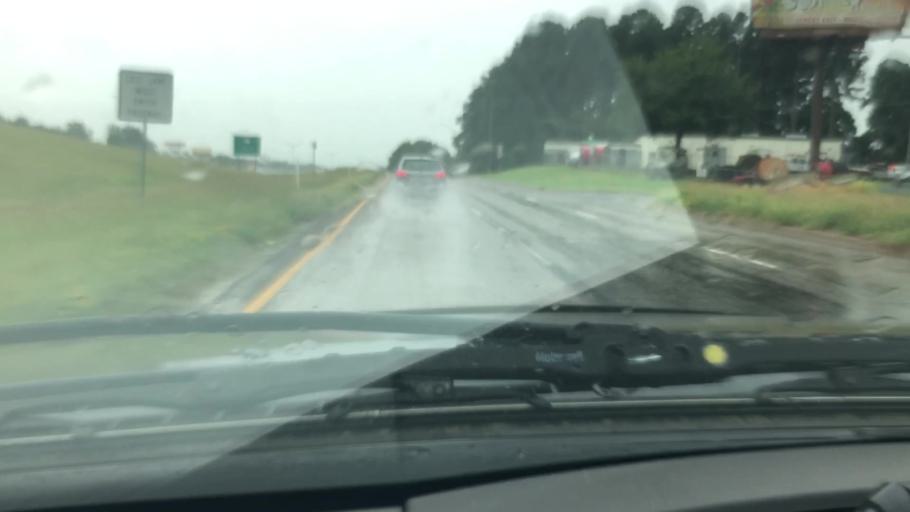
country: US
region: Texas
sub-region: Bowie County
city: Wake Village
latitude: 33.4299
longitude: -94.0970
